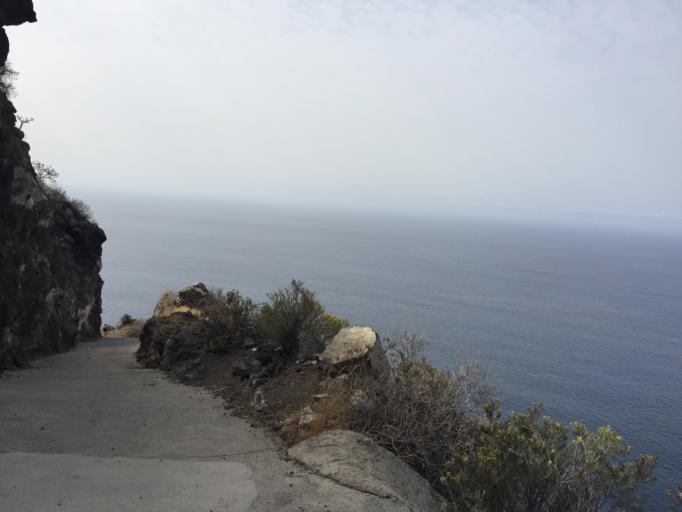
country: ES
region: Canary Islands
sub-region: Provincia de Santa Cruz de Tenerife
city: Tijarafe
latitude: 28.7174
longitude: -17.9782
